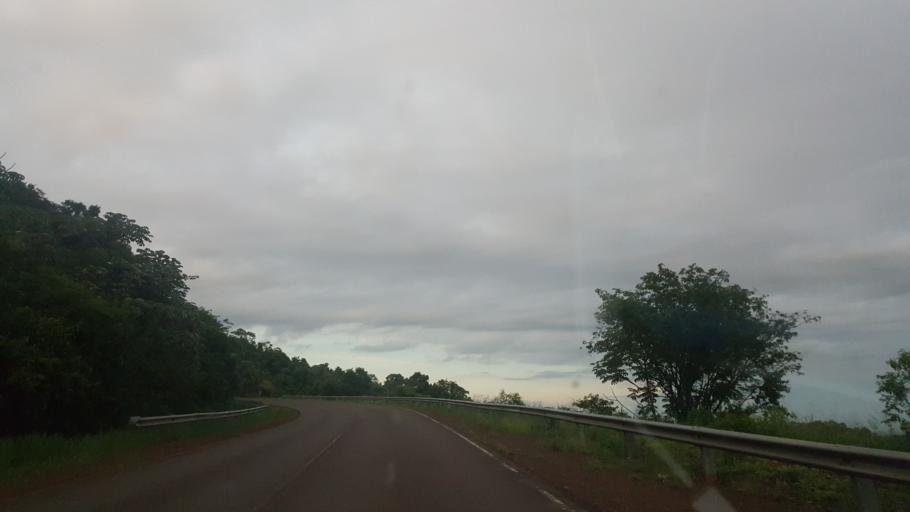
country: AR
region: Misiones
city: Dos de Mayo
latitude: -26.9079
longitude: -54.7400
